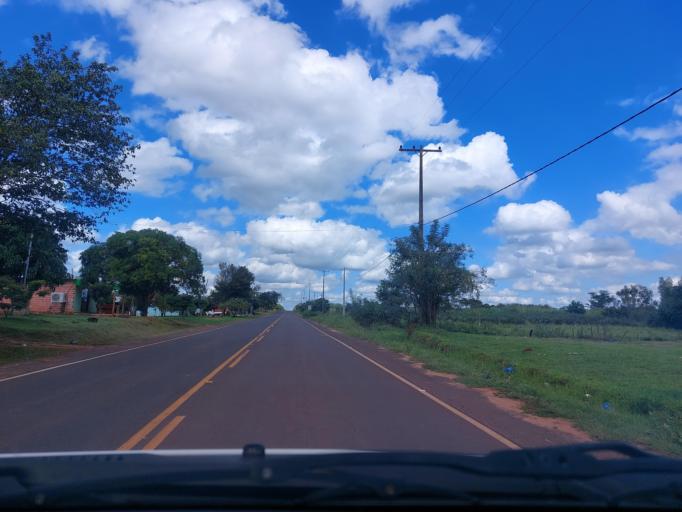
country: PY
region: San Pedro
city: Guayaybi
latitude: -24.5696
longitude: -56.5196
